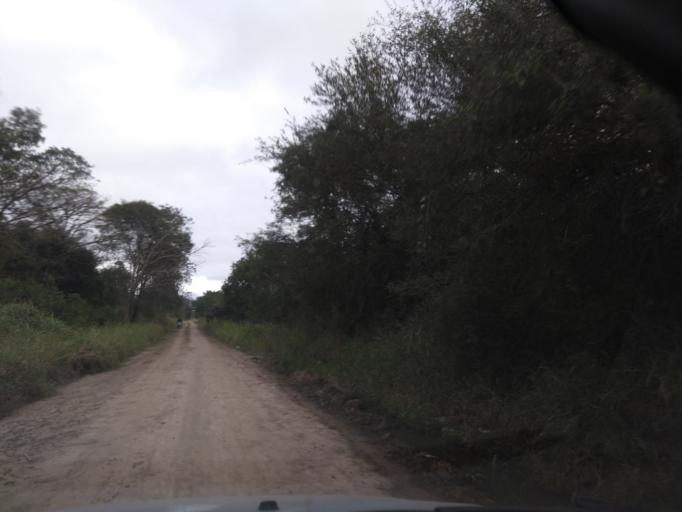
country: AR
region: Chaco
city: Barranqueras
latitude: -27.4349
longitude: -58.9425
